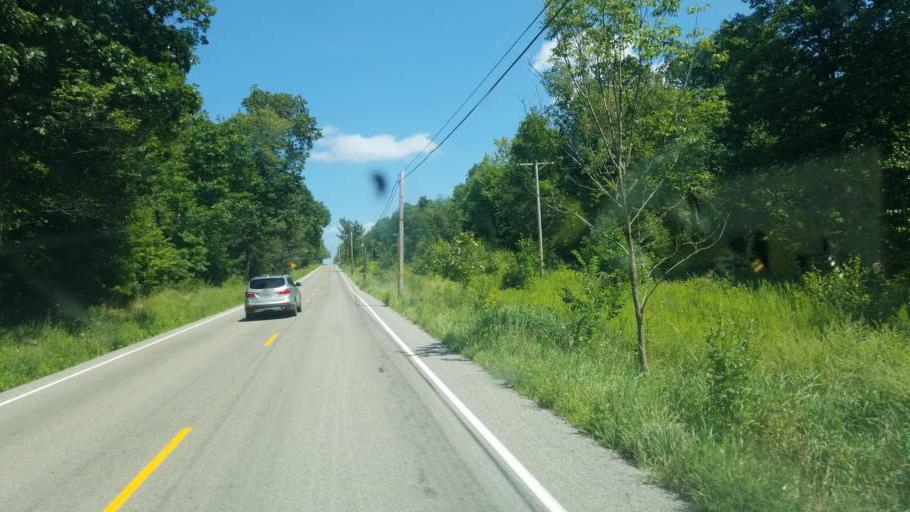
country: US
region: Pennsylvania
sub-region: Clarion County
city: Knox
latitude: 41.1051
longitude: -79.6401
